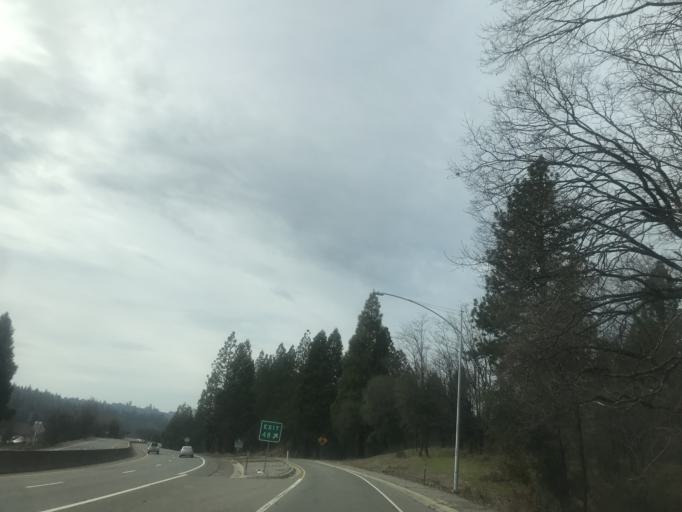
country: US
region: California
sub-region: El Dorado County
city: Placerville
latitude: 38.7344
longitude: -120.7752
